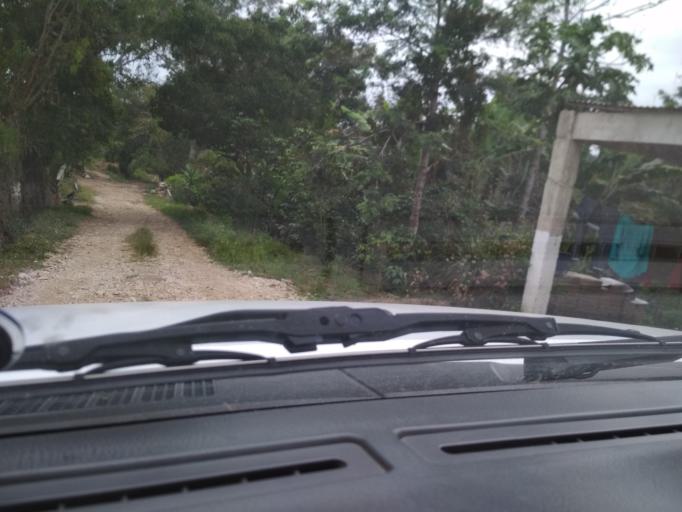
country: MX
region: Veracruz
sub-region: Emiliano Zapata
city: Dos Rios
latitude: 19.5363
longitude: -96.7995
